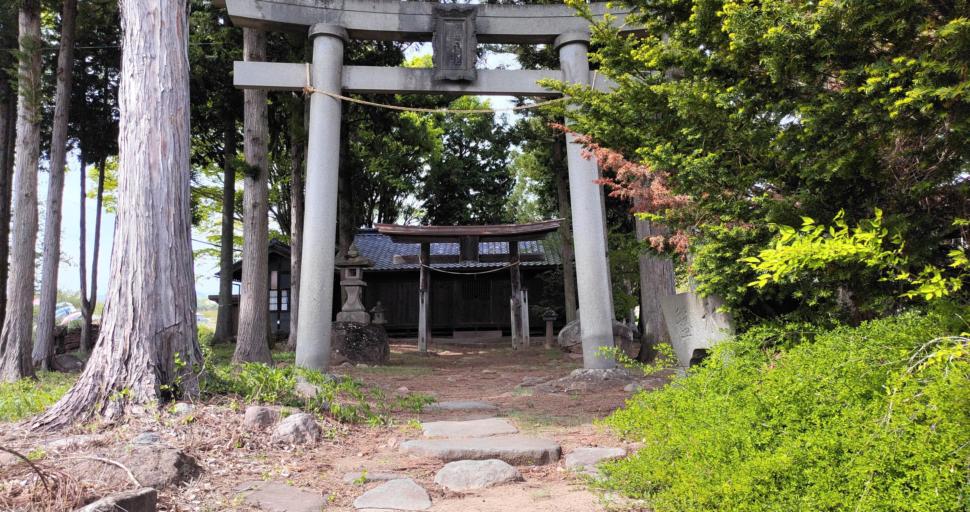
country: JP
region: Nagano
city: Komoro
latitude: 36.3541
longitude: 138.3642
